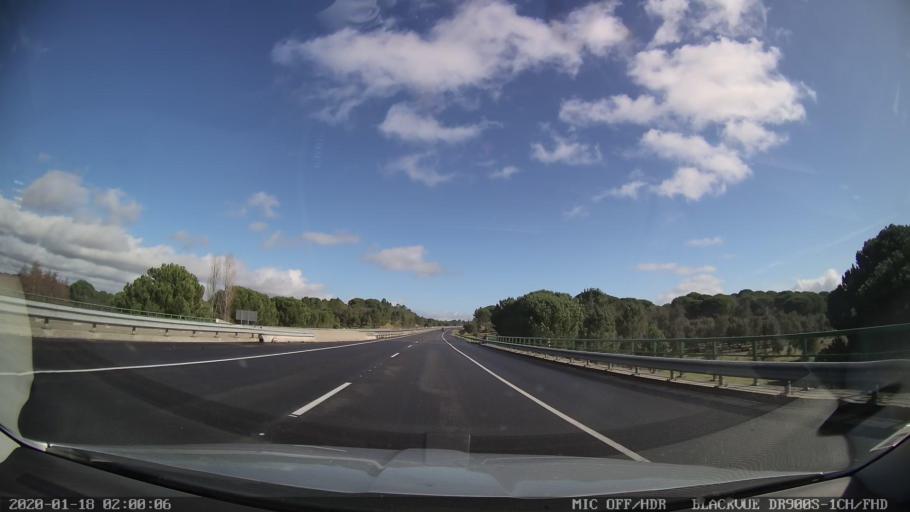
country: PT
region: Evora
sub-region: Vendas Novas
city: Vendas Novas
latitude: 38.6324
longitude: -8.5386
